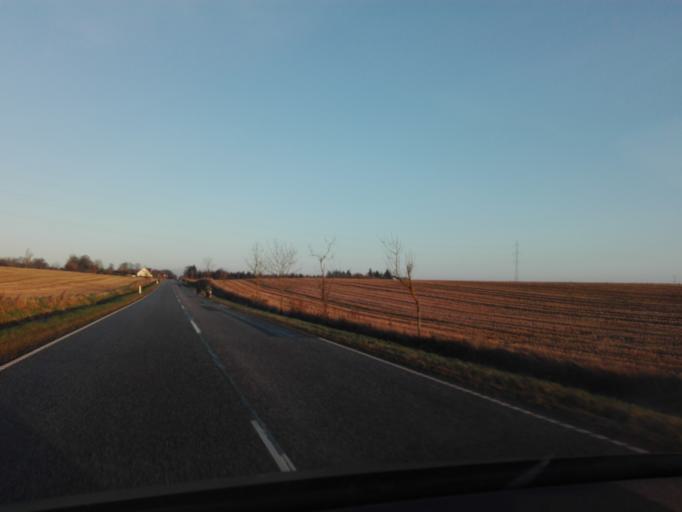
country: DK
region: Central Jutland
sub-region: Skanderborg Kommune
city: Galten
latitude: 56.1758
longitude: 9.8763
